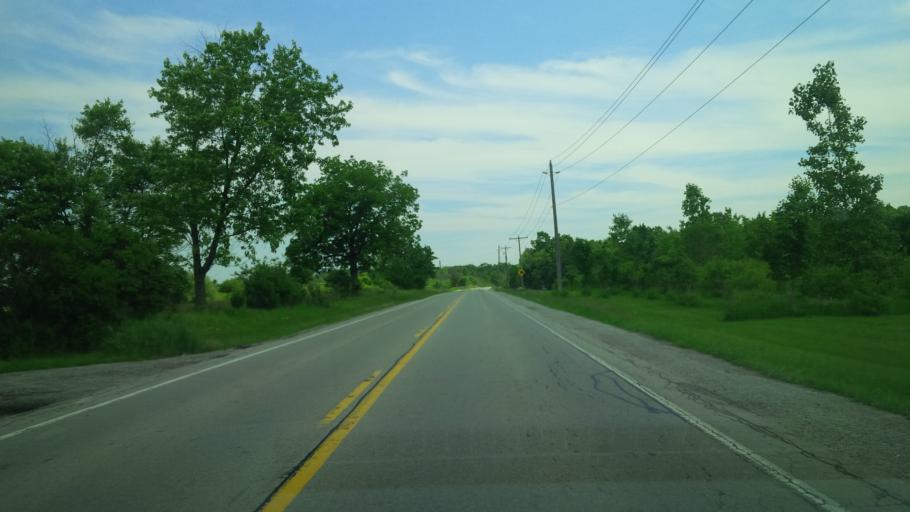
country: CA
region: Ontario
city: Burlington
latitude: 43.4379
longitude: -79.8558
